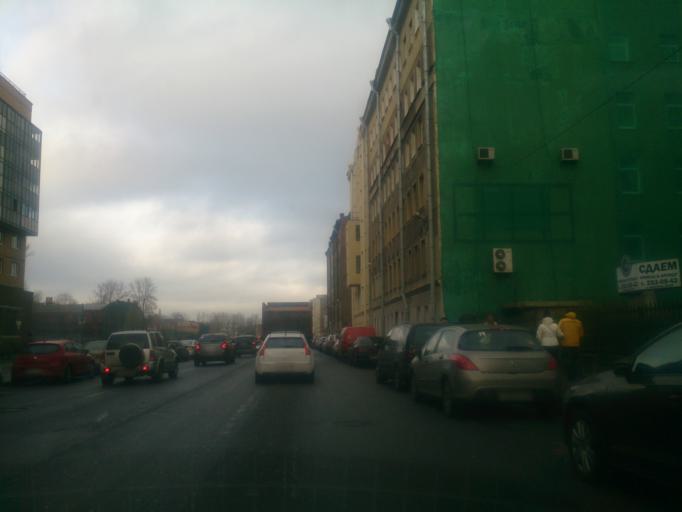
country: RU
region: St.-Petersburg
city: Admiralteisky
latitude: 59.9052
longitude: 30.2922
